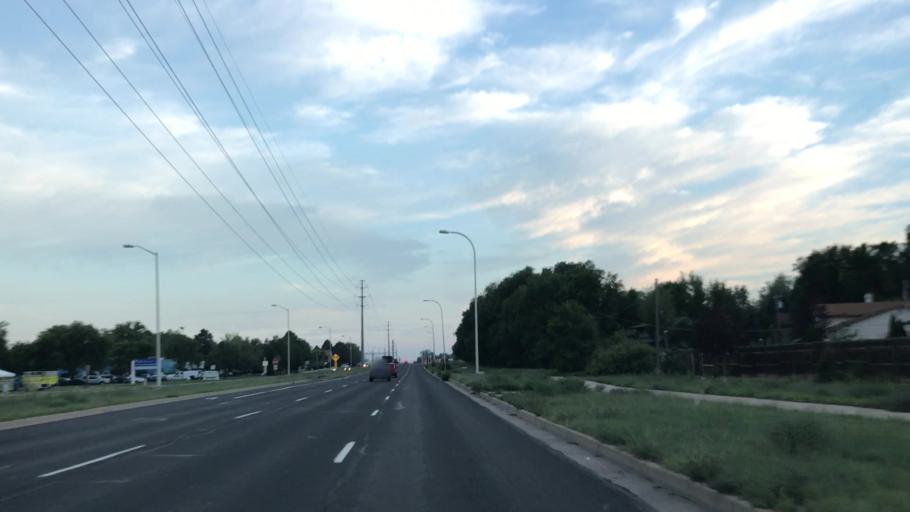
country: US
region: Colorado
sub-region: El Paso County
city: Cimarron Hills
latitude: 38.8656
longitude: -104.7573
